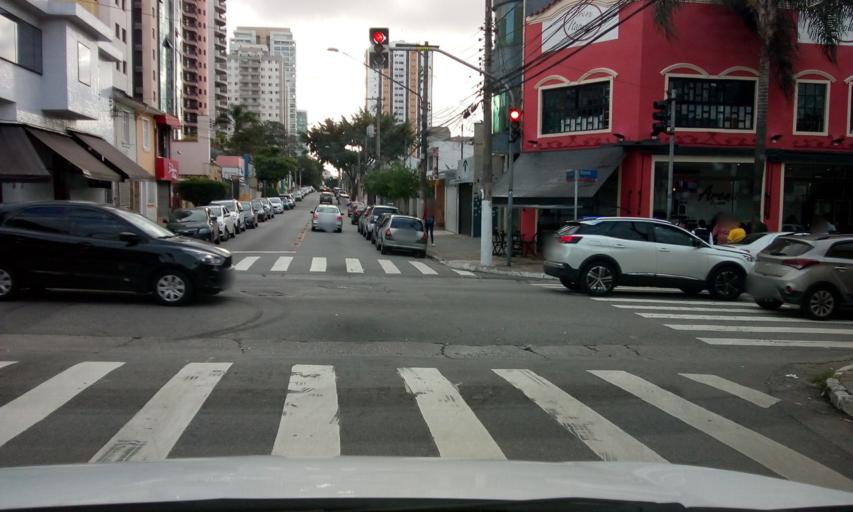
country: BR
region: Sao Paulo
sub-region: Sao Paulo
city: Sao Paulo
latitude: -23.5456
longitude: -46.5661
